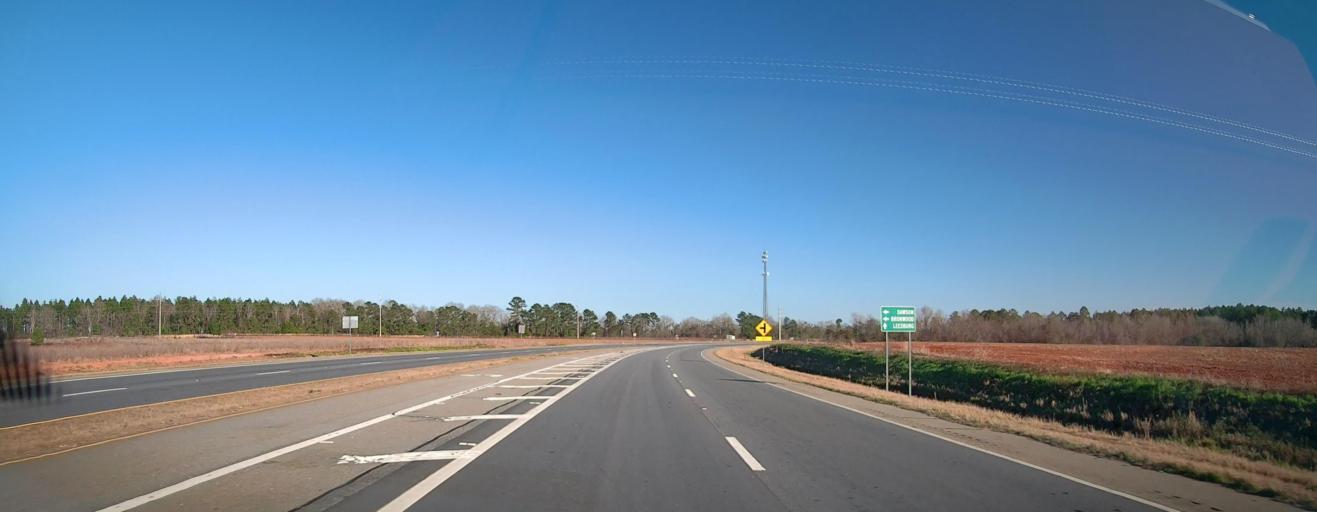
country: US
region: Georgia
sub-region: Lee County
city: Leesburg
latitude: 31.8916
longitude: -84.2519
